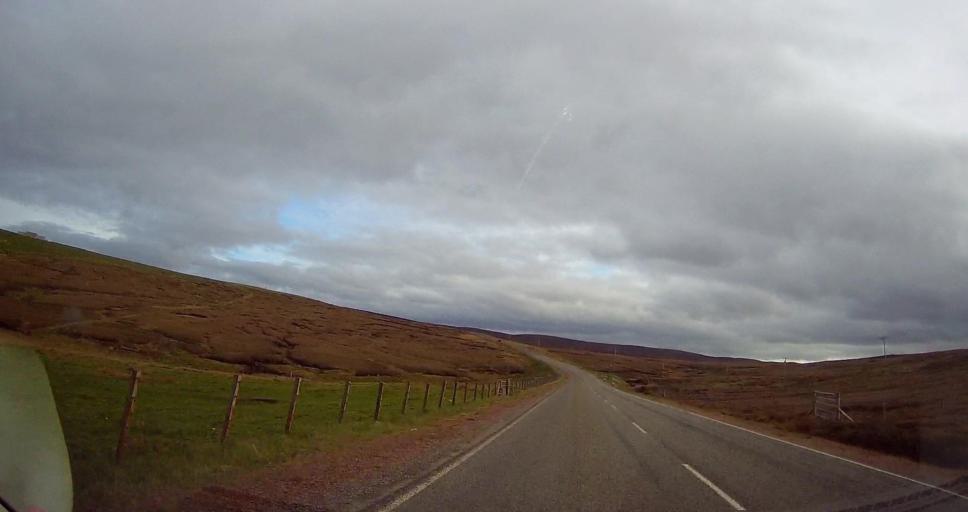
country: GB
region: Scotland
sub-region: Shetland Islands
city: Lerwick
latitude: 60.4565
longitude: -1.2114
